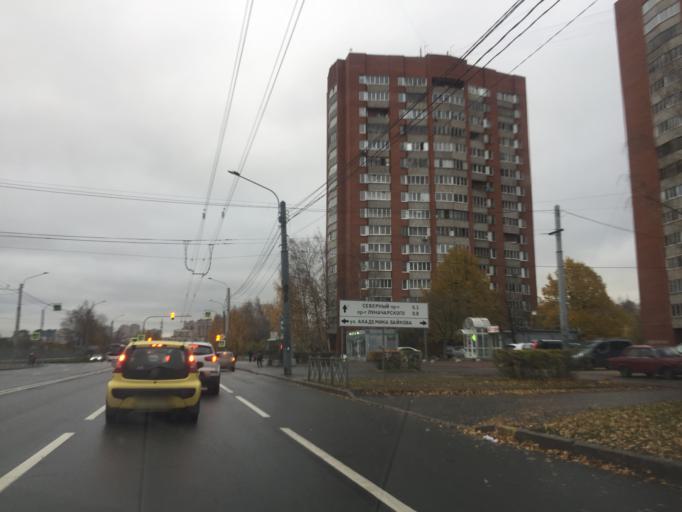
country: RU
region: Leningrad
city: Akademicheskoe
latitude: 60.0247
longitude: 30.3823
